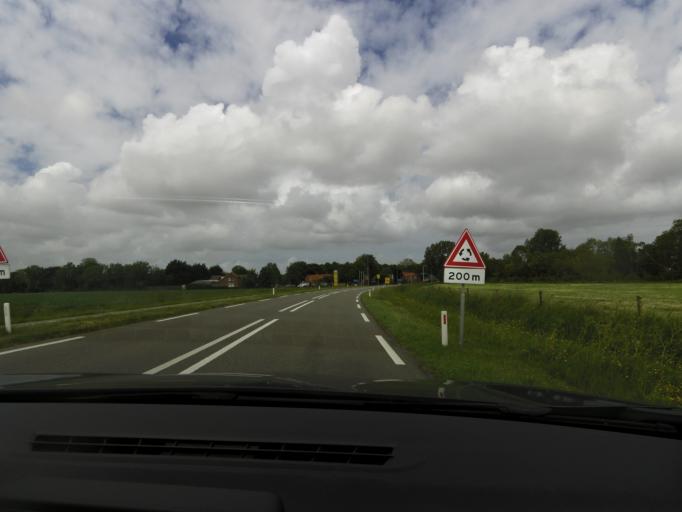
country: NL
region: Zeeland
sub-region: Schouwen-Duiveland
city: Scharendijke
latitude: 51.6915
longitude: 3.9356
